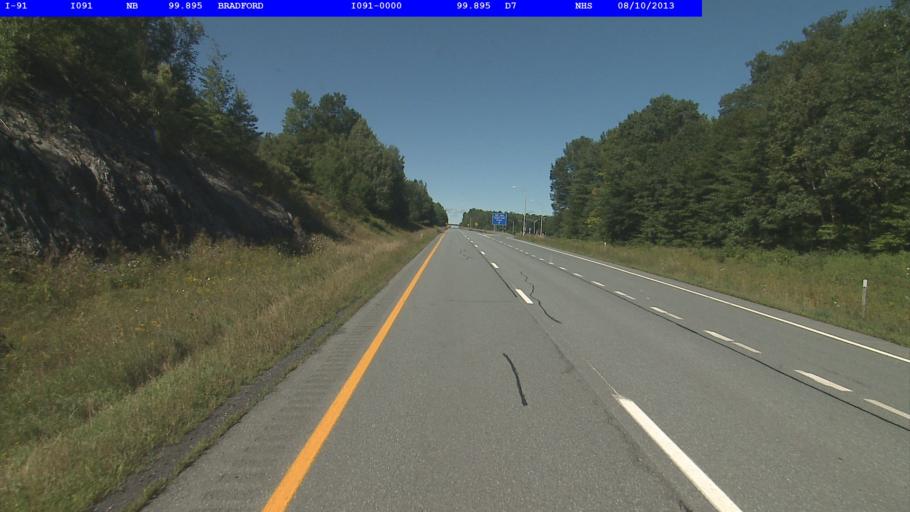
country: US
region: New Hampshire
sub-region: Grafton County
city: Haverhill
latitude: 44.0137
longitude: -72.1221
